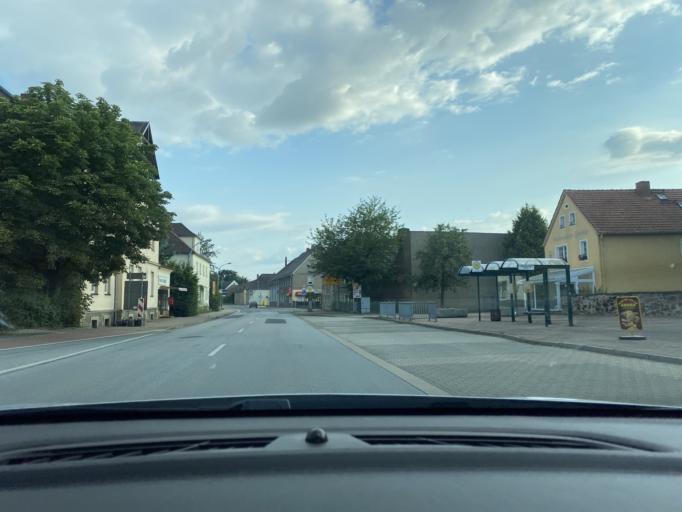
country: DE
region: Saxony
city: Konigswartha
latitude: 51.3099
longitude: 14.3287
